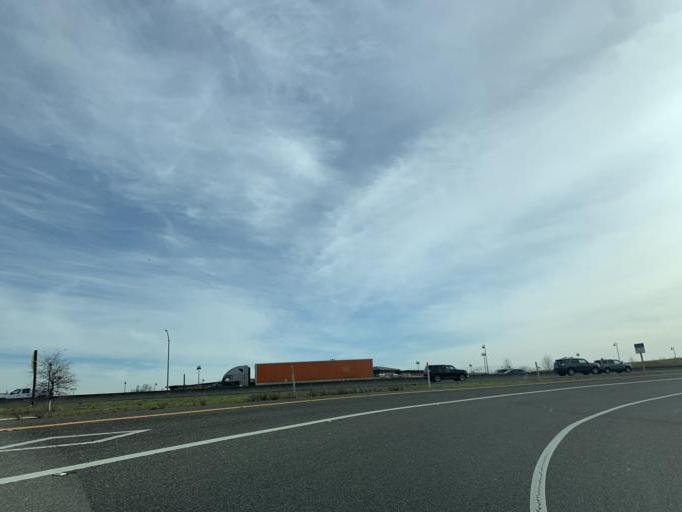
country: US
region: California
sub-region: Placer County
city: Loomis
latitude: 38.8049
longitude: -121.2043
